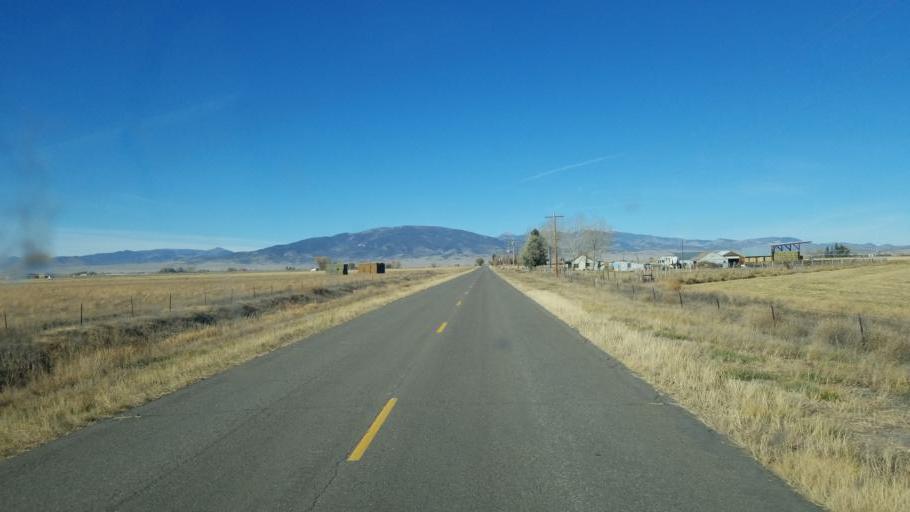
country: US
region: Colorado
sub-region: Rio Grande County
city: Monte Vista
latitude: 37.4591
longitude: -106.0638
